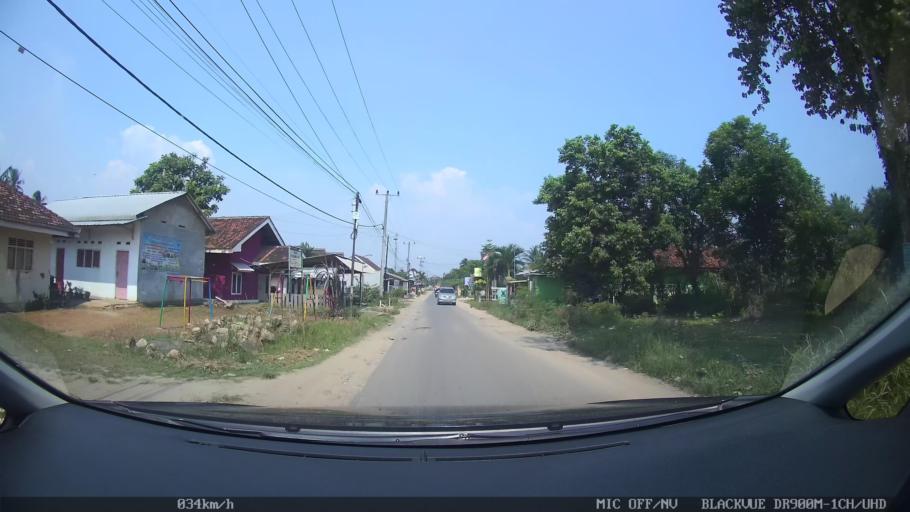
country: ID
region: Lampung
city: Natar
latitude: -5.3094
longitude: 105.2049
